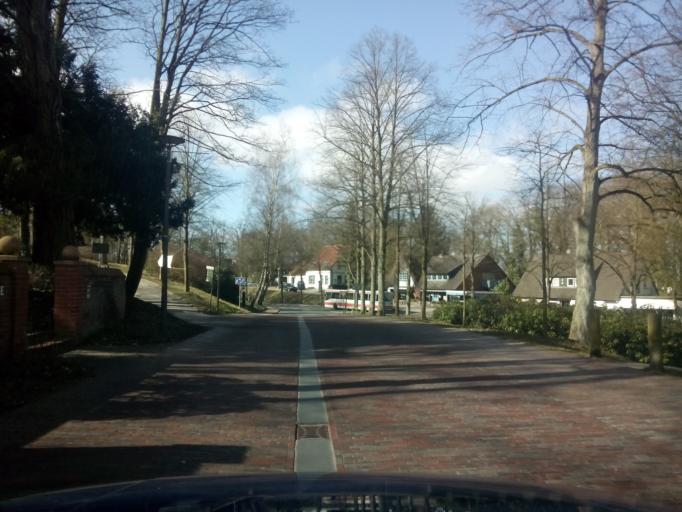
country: DE
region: Lower Saxony
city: Worpswede
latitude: 53.2212
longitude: 8.9230
